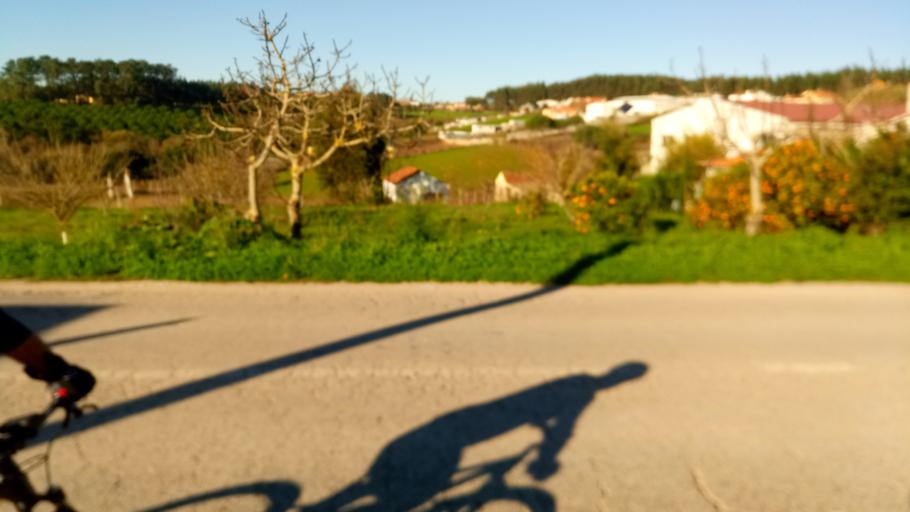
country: PT
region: Santarem
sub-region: Rio Maior
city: Rio Maior
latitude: 39.3602
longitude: -8.9987
